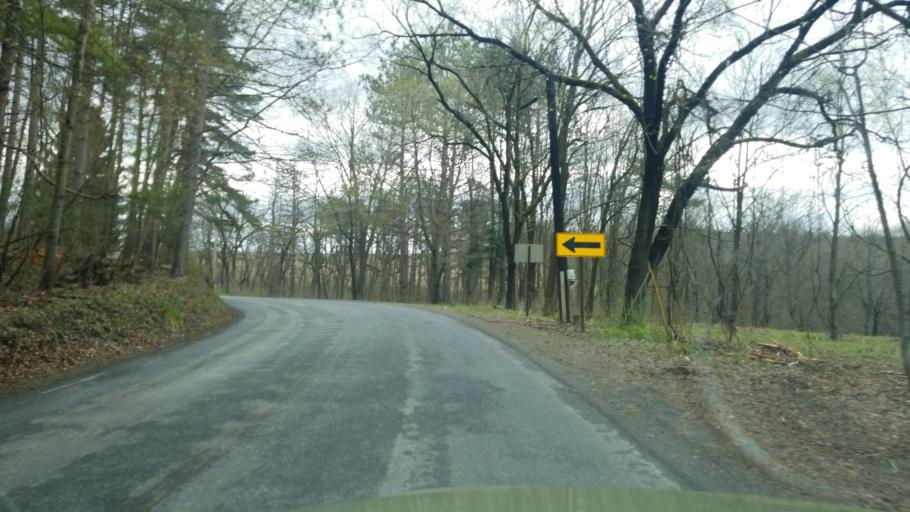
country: US
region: Pennsylvania
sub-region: Clearfield County
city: Clearfield
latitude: 41.0500
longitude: -78.4345
